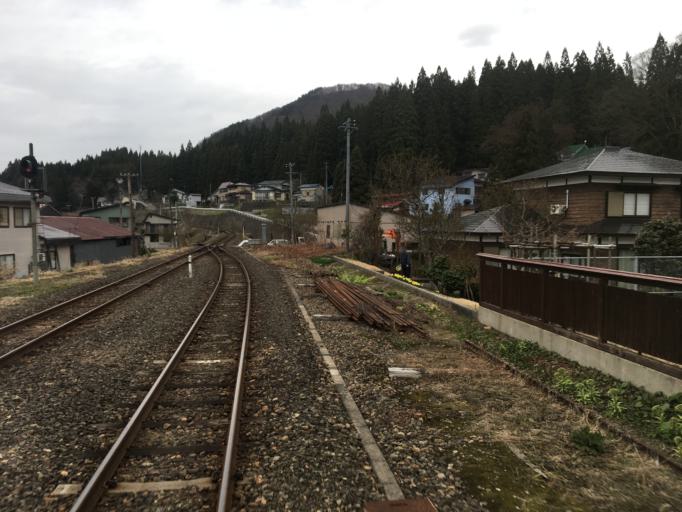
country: JP
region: Akita
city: Takanosu
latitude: 40.0620
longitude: 140.4180
